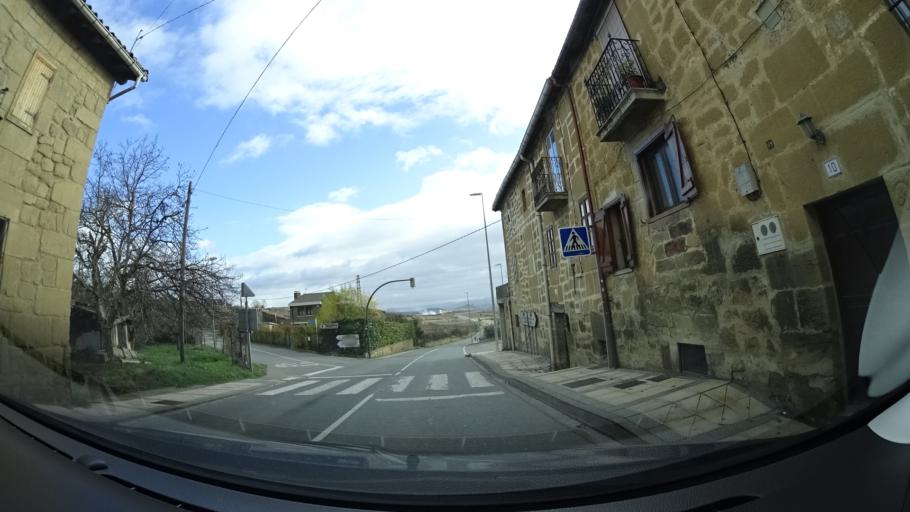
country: ES
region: Basque Country
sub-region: Provincia de Alava
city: Labastida
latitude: 42.5887
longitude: -2.7901
